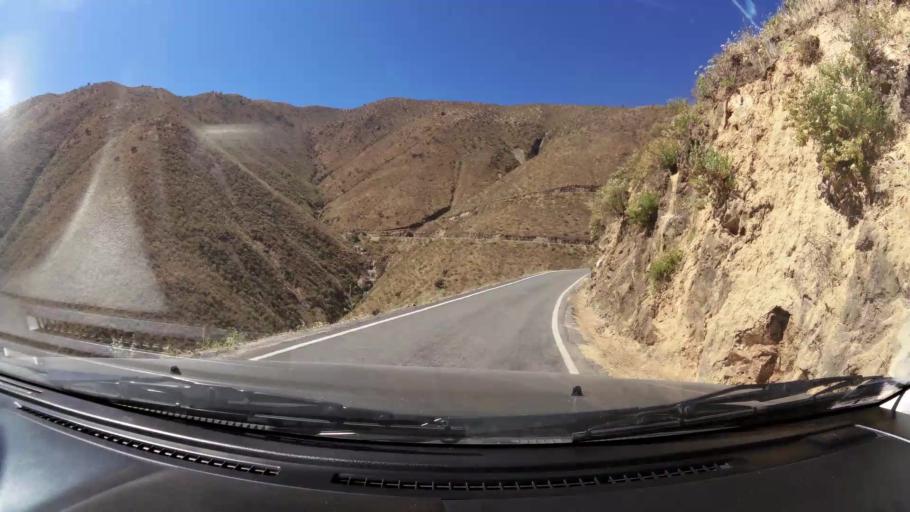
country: PE
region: Ica
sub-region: Provincia de Pisco
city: Huancano
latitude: -13.7219
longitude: -75.4539
